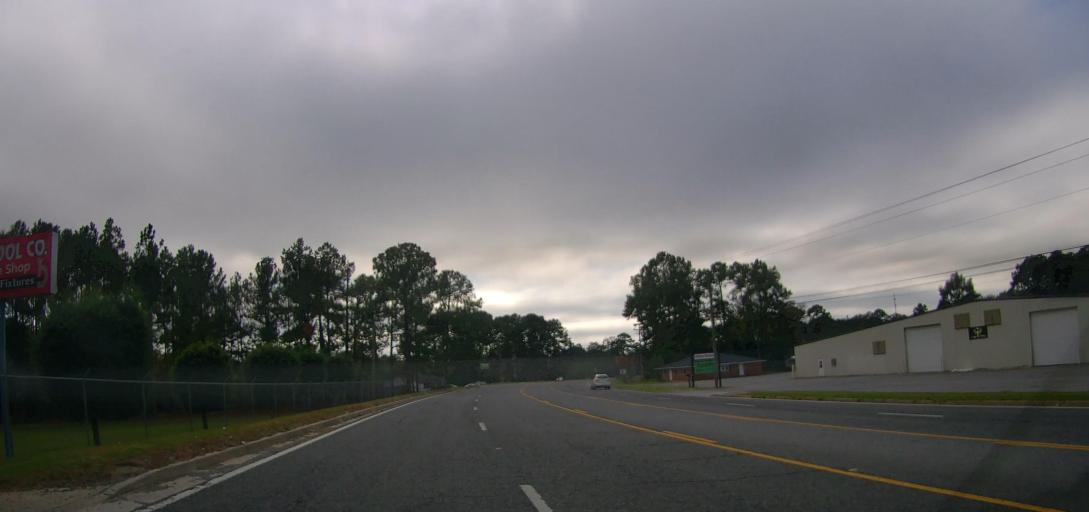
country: US
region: Georgia
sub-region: Tift County
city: Unionville
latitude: 31.3966
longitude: -83.5362
